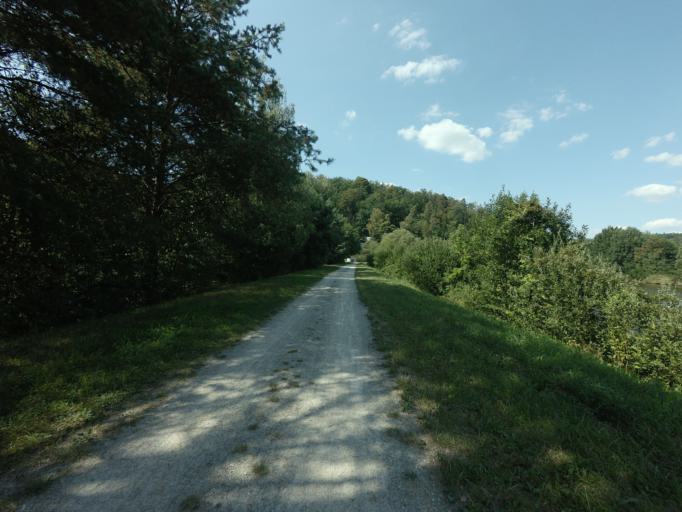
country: CZ
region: Jihocesky
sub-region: Okres Ceske Budejovice
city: Hluboka nad Vltavou
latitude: 49.0568
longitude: 14.4429
